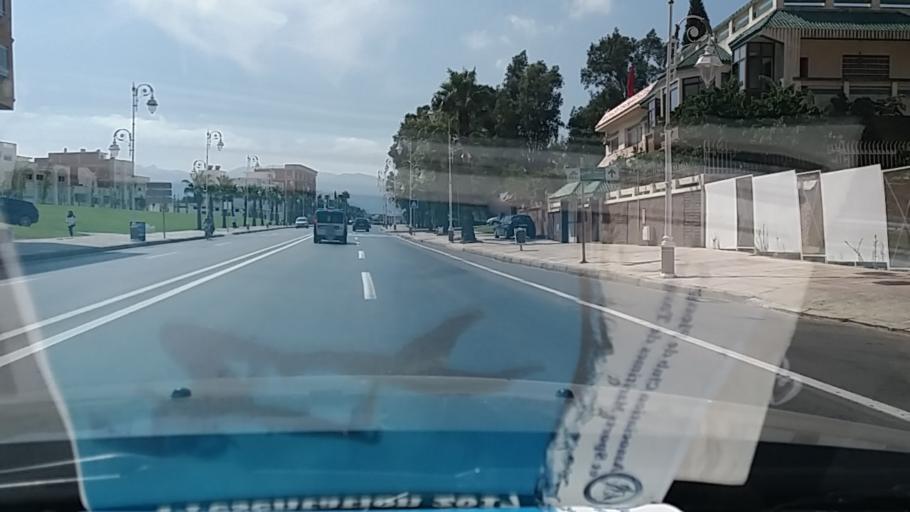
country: MA
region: Tanger-Tetouan
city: Tetouan
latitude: 35.5961
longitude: -5.3402
